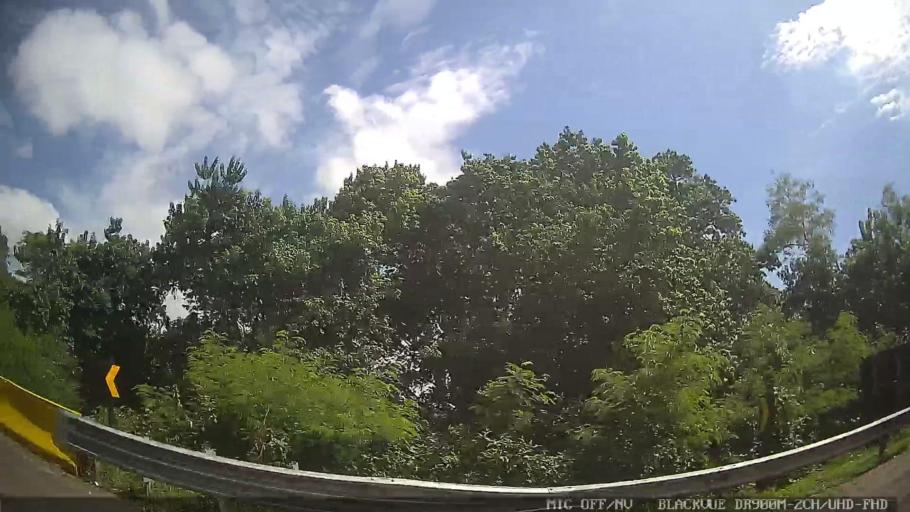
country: BR
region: Sao Paulo
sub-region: Tiete
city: Tiete
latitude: -23.1161
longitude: -47.7271
